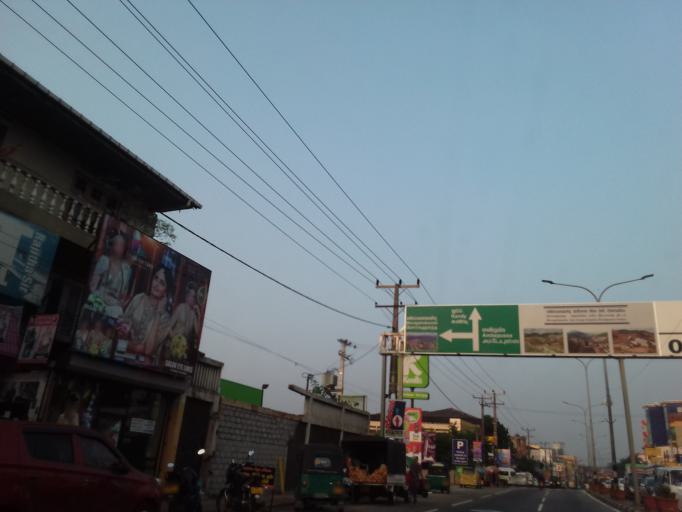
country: LK
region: Western
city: Kelaniya
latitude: 6.9820
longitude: 79.9308
